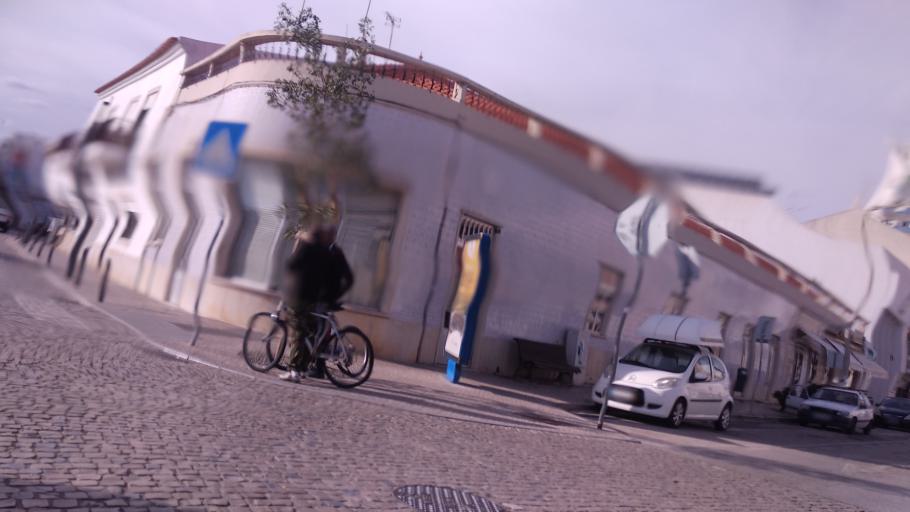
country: PT
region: Faro
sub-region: Sao Bras de Alportel
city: Sao Bras de Alportel
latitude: 37.1525
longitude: -7.8886
